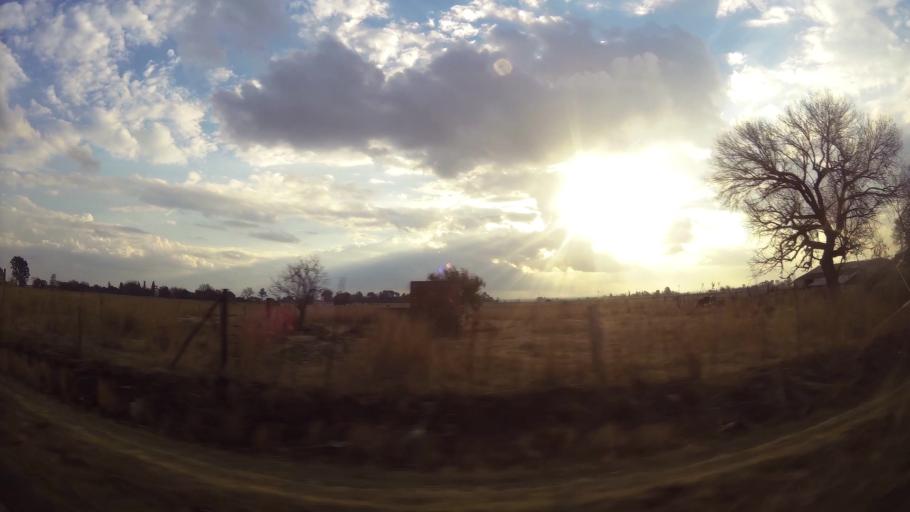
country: ZA
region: Gauteng
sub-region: Sedibeng District Municipality
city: Vanderbijlpark
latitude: -26.6338
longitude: 27.8079
